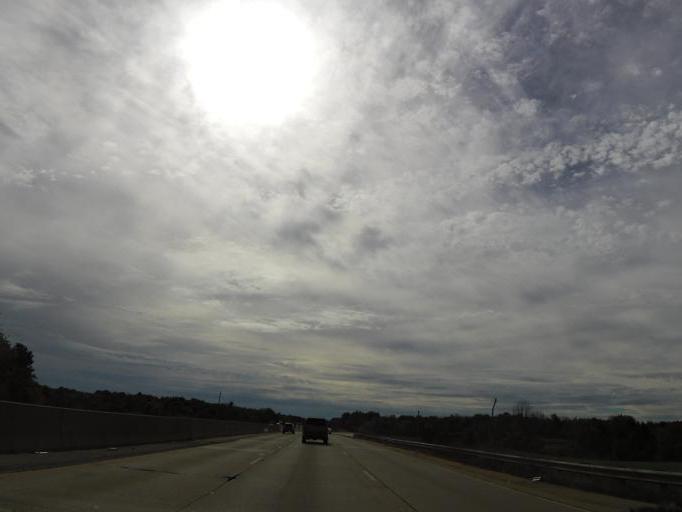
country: US
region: Ohio
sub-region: Summit County
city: Silver Lake
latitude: 41.2043
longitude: -81.4838
